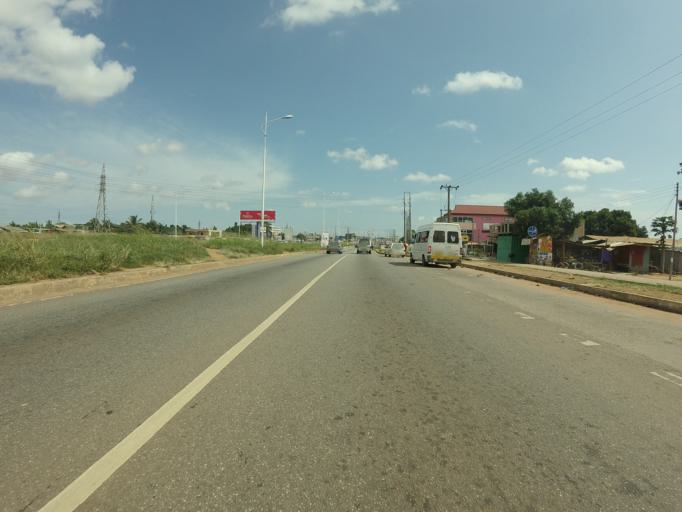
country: GH
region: Greater Accra
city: Medina Estates
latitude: 5.7108
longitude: -0.1715
